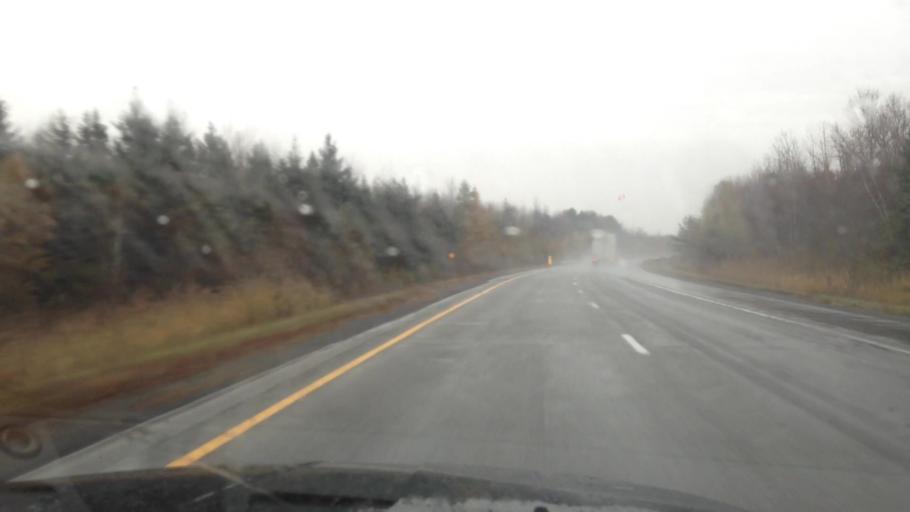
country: CA
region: Ontario
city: Casselman
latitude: 45.3166
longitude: -75.1642
